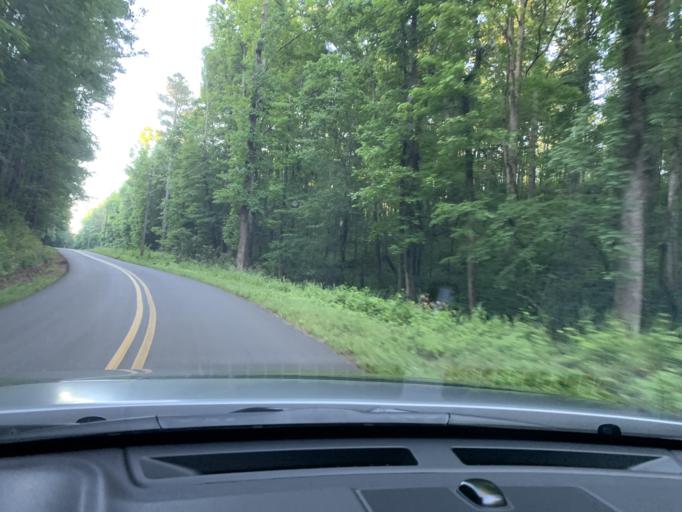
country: US
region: Georgia
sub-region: Bartow County
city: Rydal
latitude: 34.2398
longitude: -84.6684
